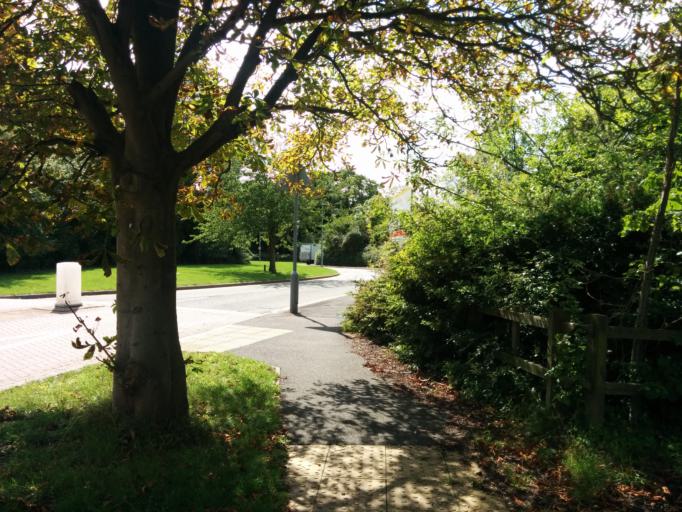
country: GB
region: England
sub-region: Cambridgeshire
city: Cambridge
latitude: 52.2069
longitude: 0.0989
